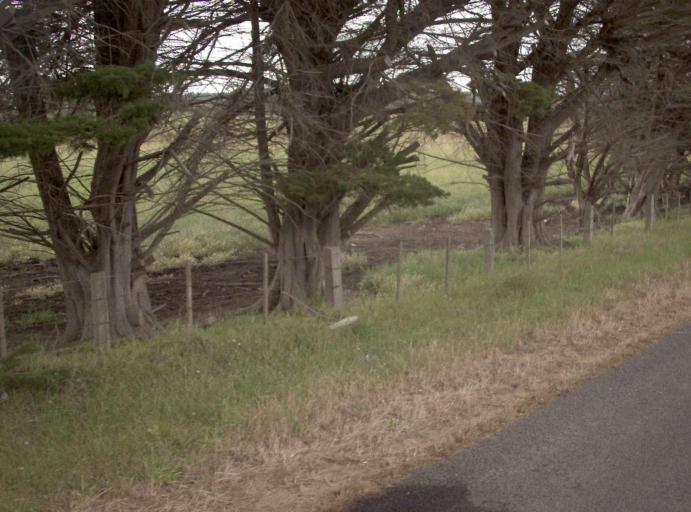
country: AU
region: Victoria
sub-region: Baw Baw
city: Warragul
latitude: -38.5106
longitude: 145.9518
